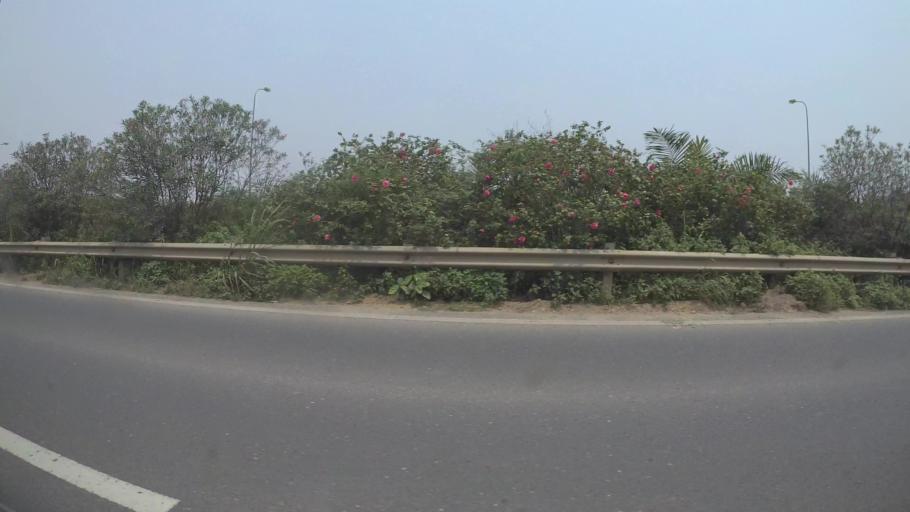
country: VN
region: Ha Noi
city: Lien Quan
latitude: 20.9893
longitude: 105.5645
